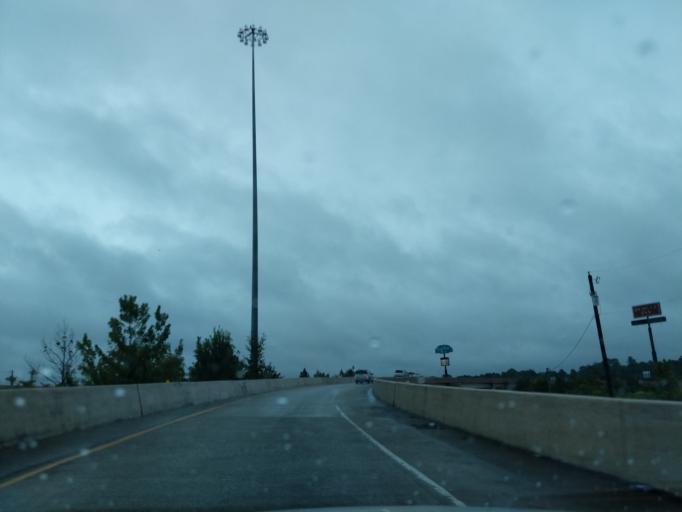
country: US
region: Texas
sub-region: Angelina County
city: Lufkin
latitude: 31.3085
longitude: -94.7262
